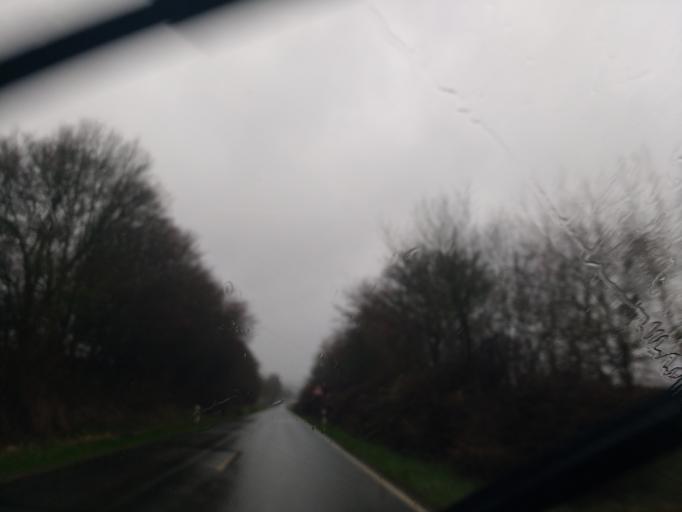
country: DE
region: Schleswig-Holstein
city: Blekendorf
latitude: 54.2967
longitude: 10.6722
